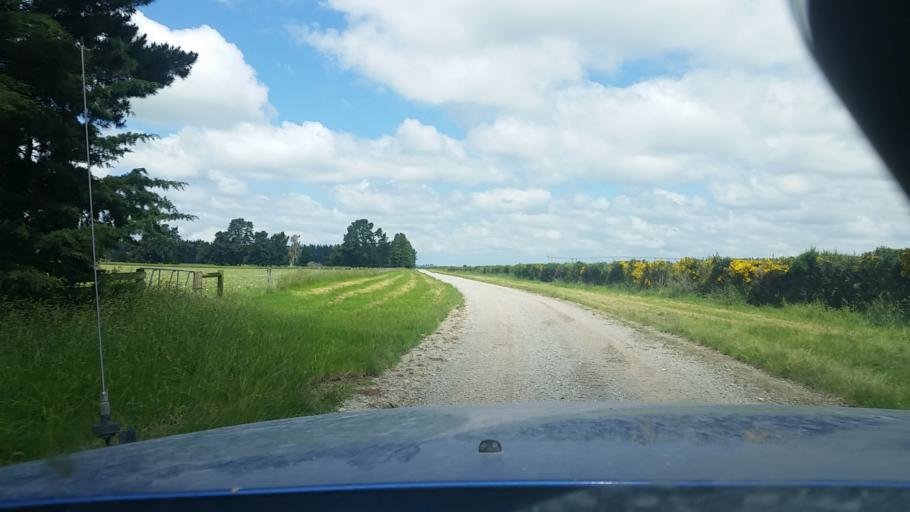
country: NZ
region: Canterbury
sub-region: Ashburton District
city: Tinwald
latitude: -43.8825
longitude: 171.3317
